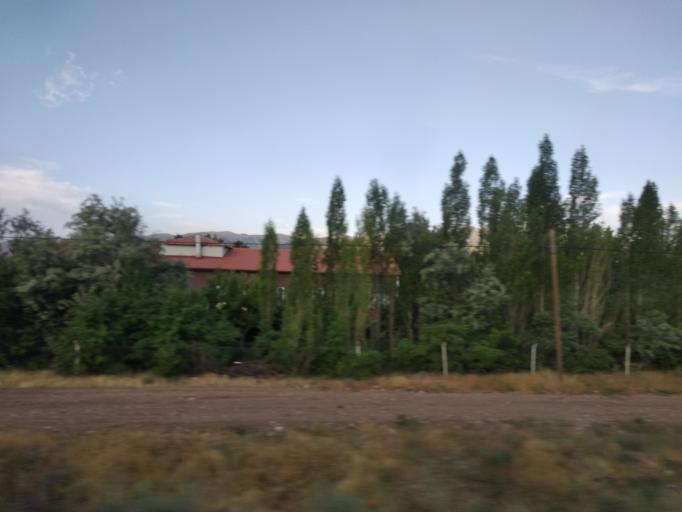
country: TR
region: Erzincan
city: Catalarmut
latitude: 39.8099
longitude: 39.3608
